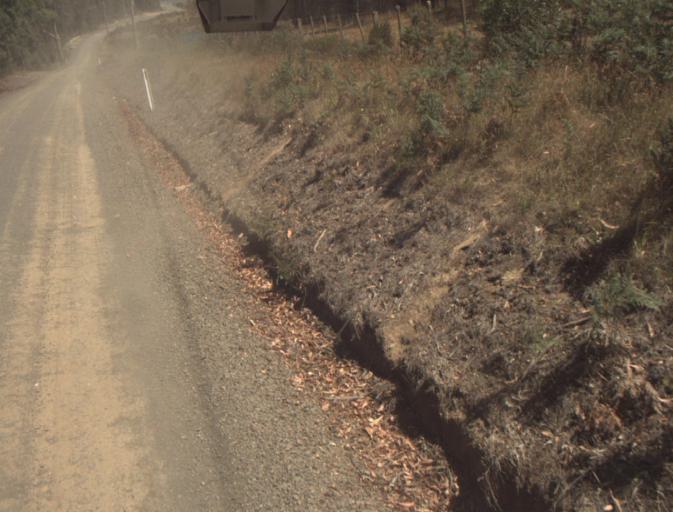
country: AU
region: Tasmania
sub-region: Launceston
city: Newstead
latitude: -41.3422
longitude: 147.3529
